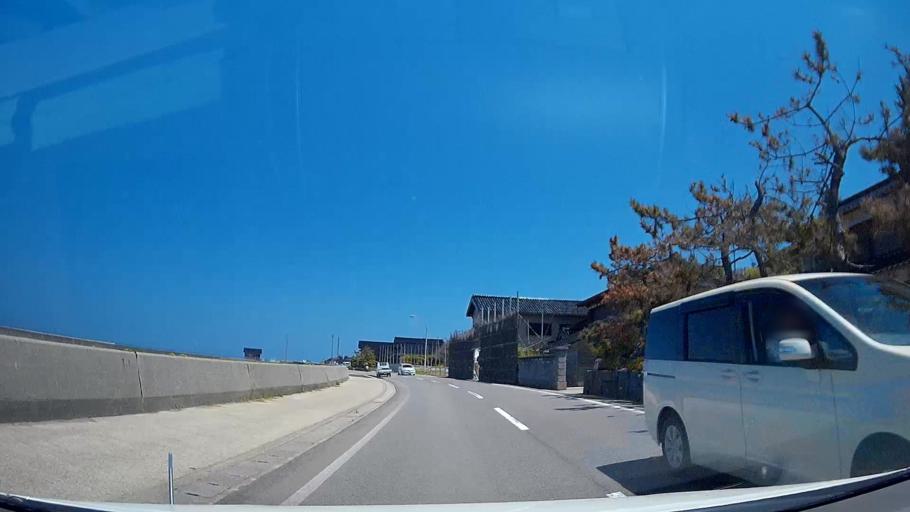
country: JP
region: Ishikawa
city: Nanao
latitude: 37.5276
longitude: 137.2864
